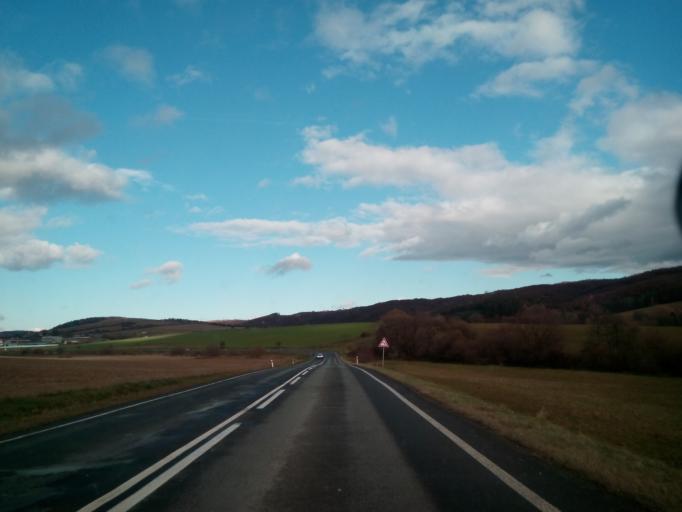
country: SK
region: Presovsky
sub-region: Okres Bardejov
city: Bardejov
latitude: 49.1993
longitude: 21.3096
